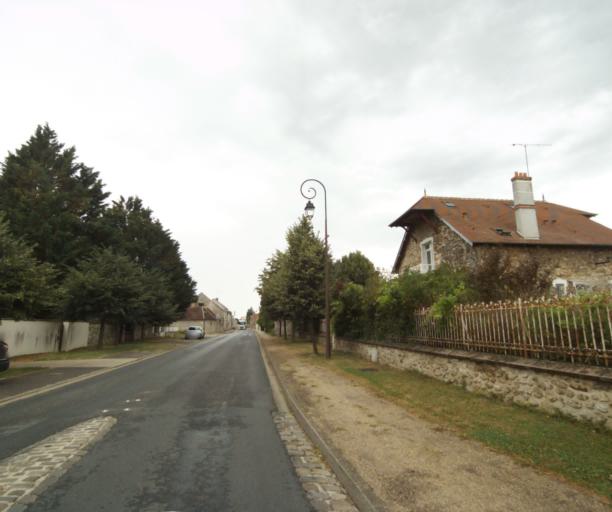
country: FR
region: Ile-de-France
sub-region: Departement de Seine-et-Marne
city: Perthes
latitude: 48.4790
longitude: 2.5603
